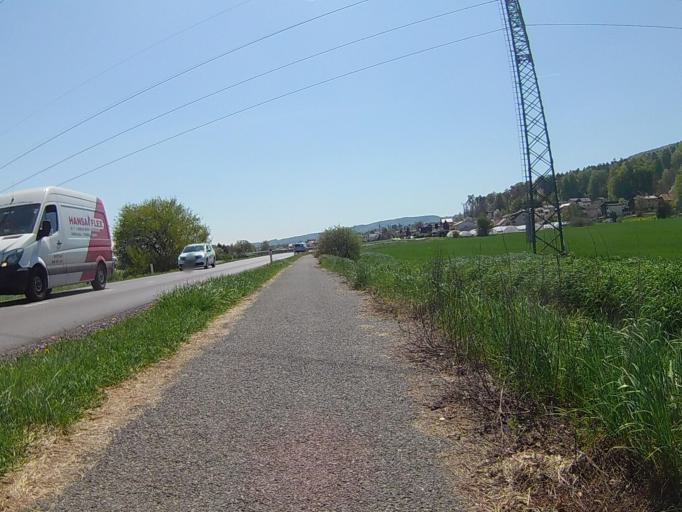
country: SI
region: Maribor
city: Razvanje
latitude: 46.5260
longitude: 15.6368
